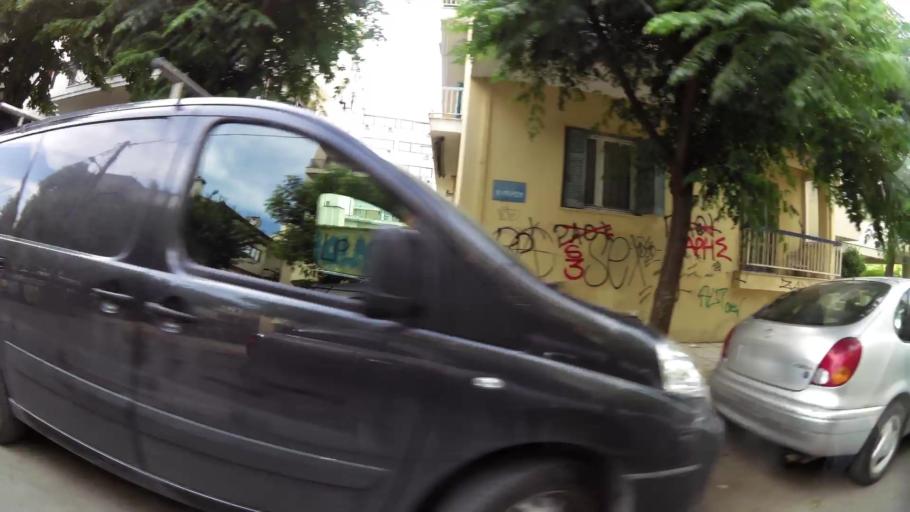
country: GR
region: Central Macedonia
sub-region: Nomos Thessalonikis
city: Kalamaria
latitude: 40.5891
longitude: 22.9554
